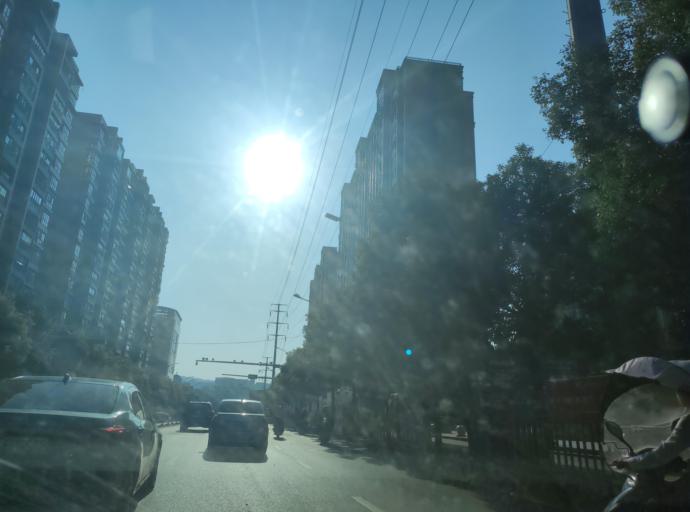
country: CN
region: Jiangxi Sheng
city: Pingxiang
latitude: 27.6336
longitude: 113.8660
